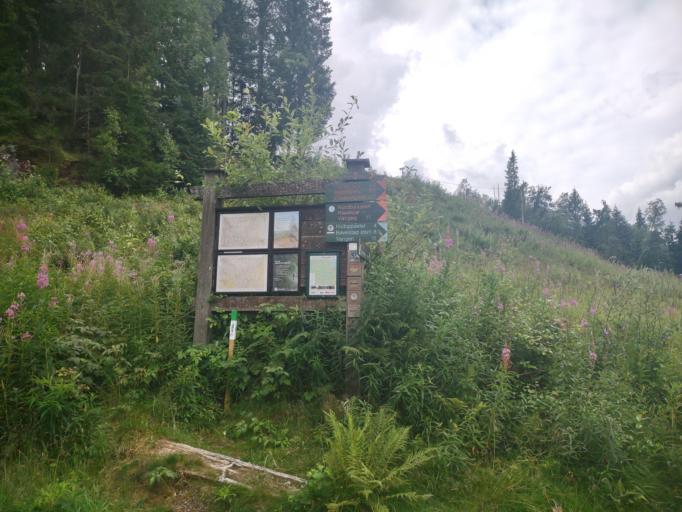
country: NO
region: Akershus
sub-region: Enebakk
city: Flateby
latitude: 59.8327
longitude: 11.1222
